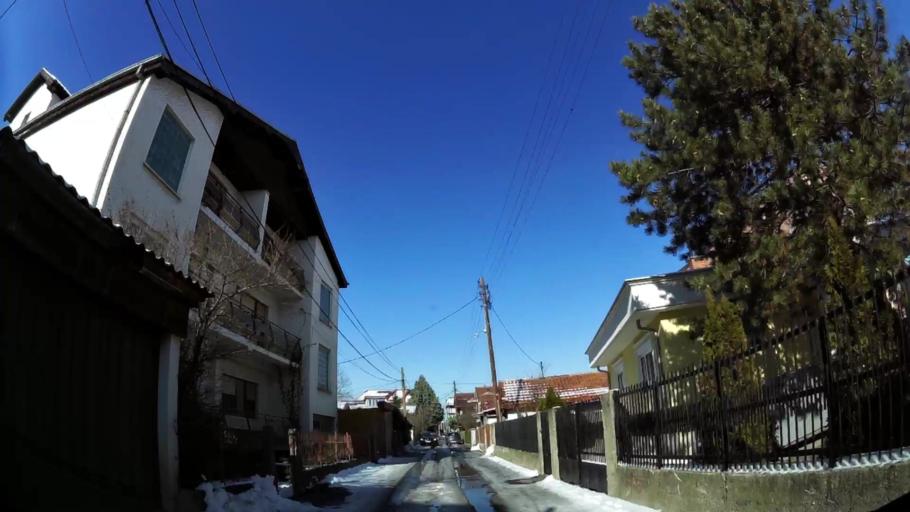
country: MK
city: Krushopek
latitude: 42.0054
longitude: 21.3594
